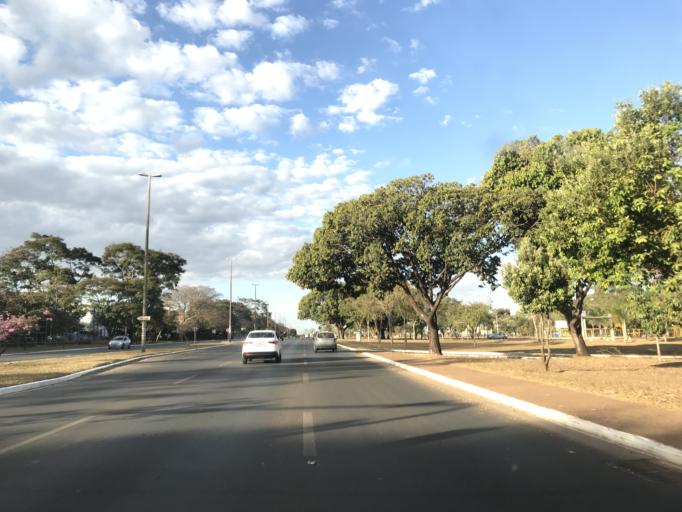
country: BR
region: Federal District
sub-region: Brasilia
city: Brasilia
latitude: -15.8310
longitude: -47.9089
